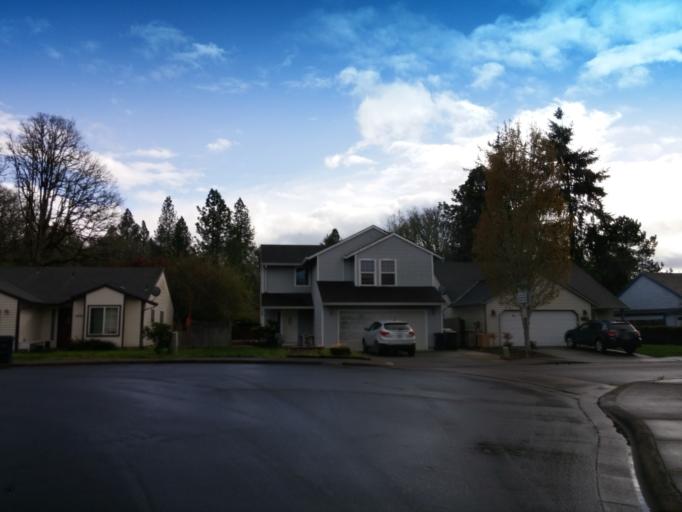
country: US
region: Oregon
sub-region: Washington County
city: Aloha
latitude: 45.5106
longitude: -122.8650
